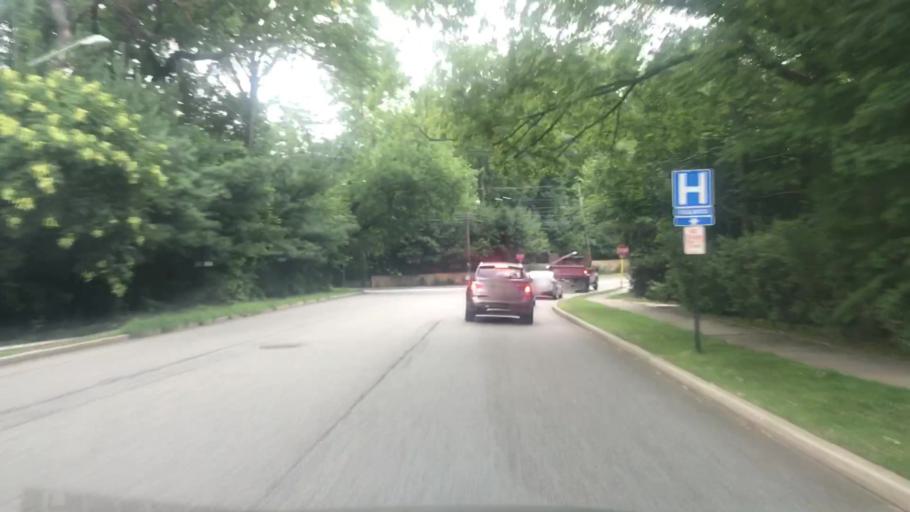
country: US
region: New Jersey
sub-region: Bergen County
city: Englewood
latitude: 40.8835
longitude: -73.9722
